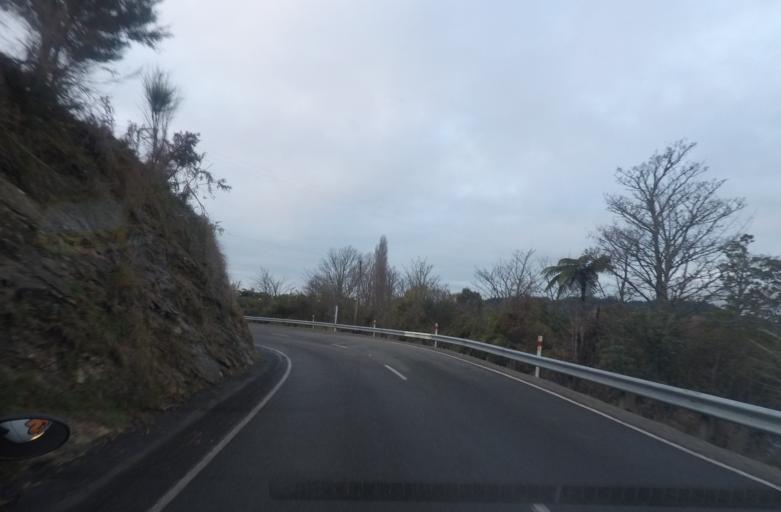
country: NZ
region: Tasman
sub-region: Tasman District
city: Takaka
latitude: -40.8319
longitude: 172.7908
